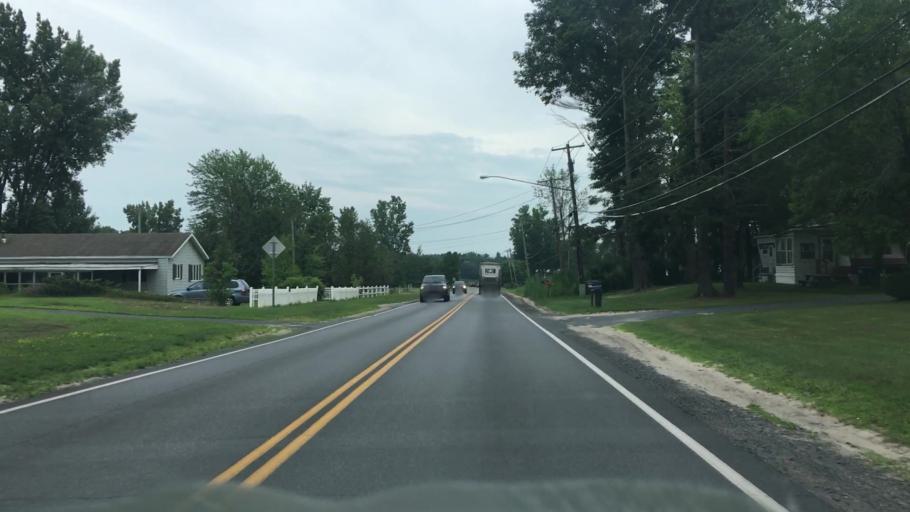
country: US
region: New York
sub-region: Clinton County
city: Plattsburgh West
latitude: 44.6738
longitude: -73.5062
